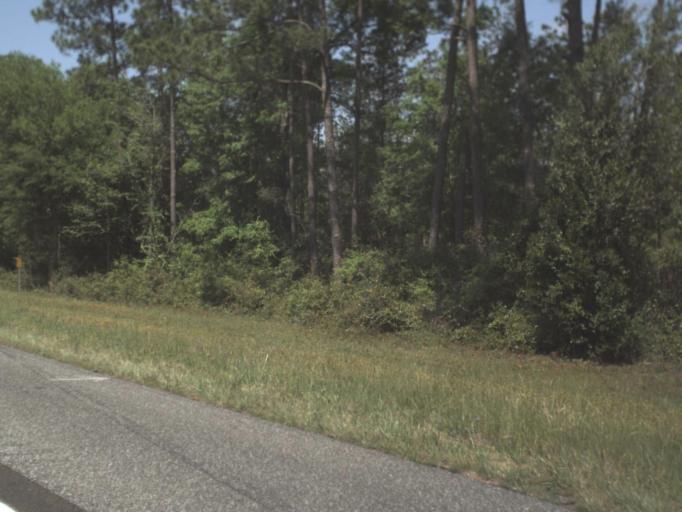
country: US
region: Florida
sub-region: Santa Rosa County
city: East Milton
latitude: 30.6394
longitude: -86.9128
